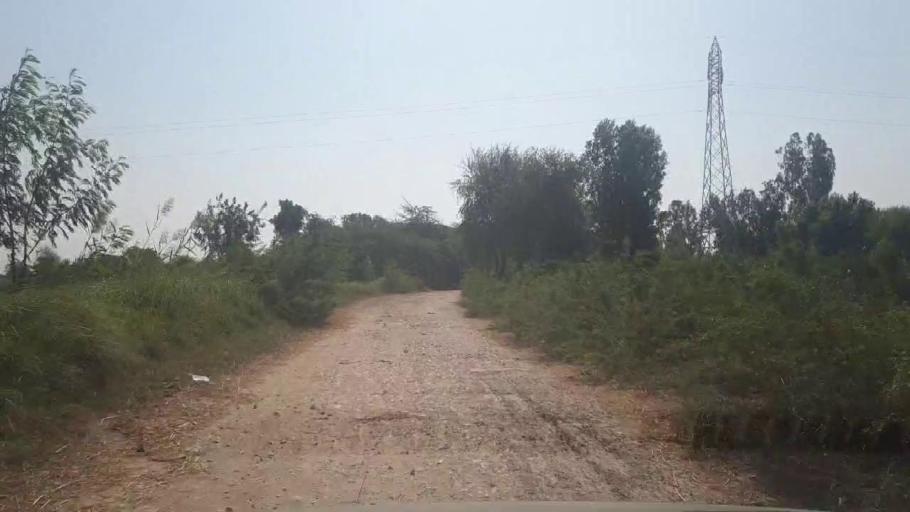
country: PK
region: Sindh
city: Badin
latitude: 24.6774
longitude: 68.8804
